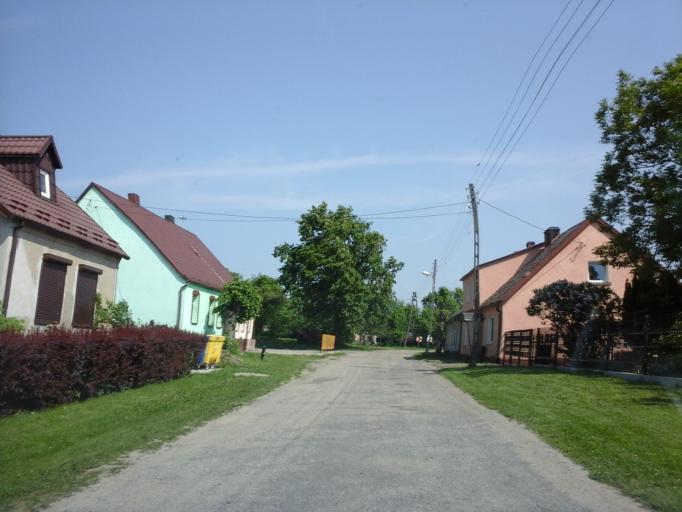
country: PL
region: West Pomeranian Voivodeship
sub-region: Powiat choszczenski
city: Recz
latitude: 53.3475
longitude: 15.5440
